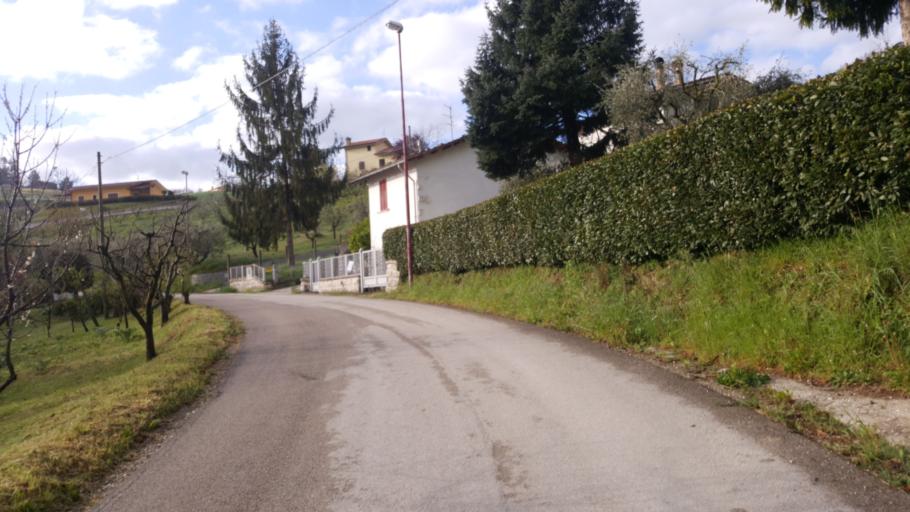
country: IT
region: The Marches
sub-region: Provincia di Ascoli Piceno
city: Venarotta
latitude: 42.8689
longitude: 13.5328
